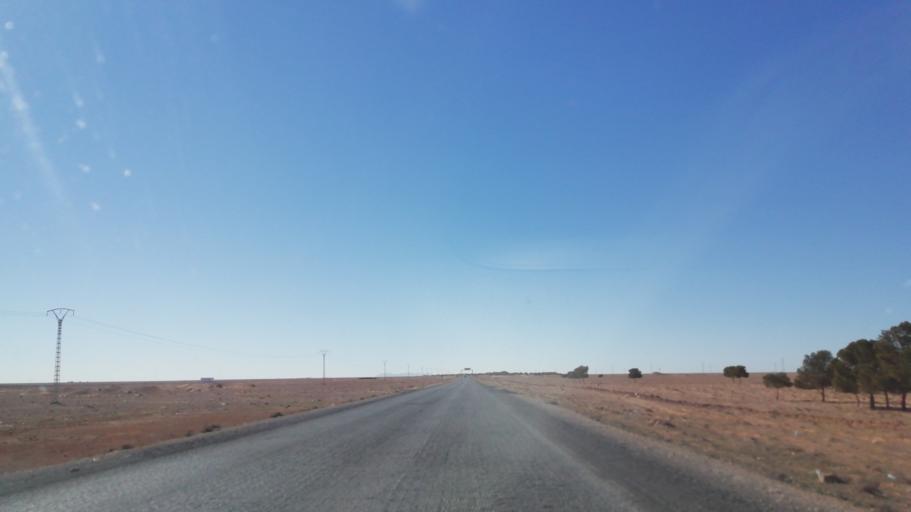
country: DZ
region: Saida
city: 'Ain el Hadjar
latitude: 34.0118
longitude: 0.0547
